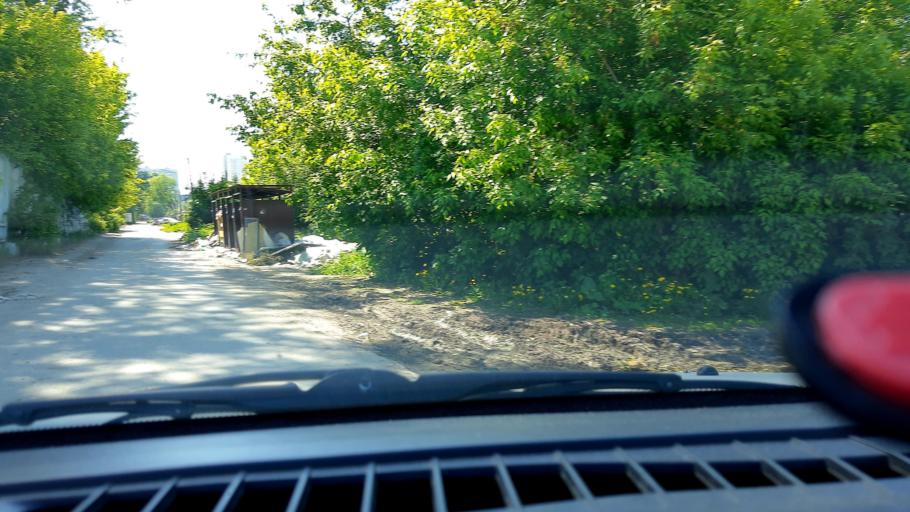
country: RU
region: Nizjnij Novgorod
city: Nizhniy Novgorod
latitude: 56.3102
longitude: 43.9173
